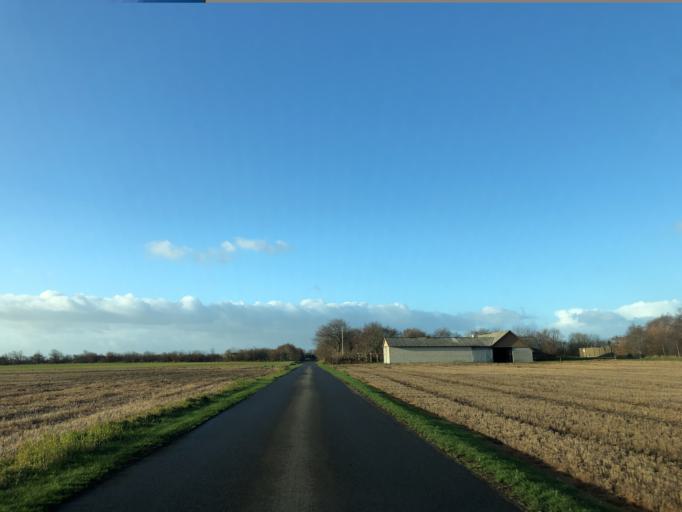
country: DK
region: Central Jutland
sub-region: Holstebro Kommune
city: Ulfborg
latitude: 56.2100
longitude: 8.2771
